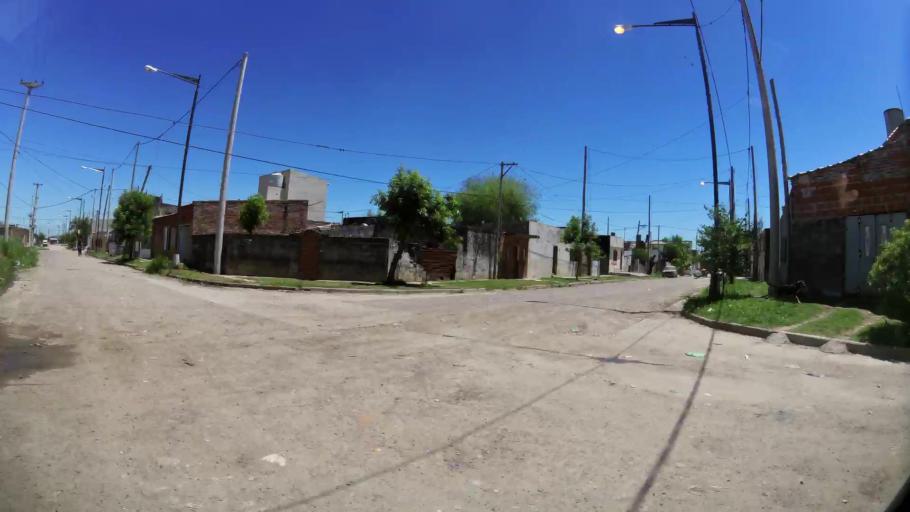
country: AR
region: Santa Fe
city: Santa Fe de la Vera Cruz
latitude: -31.6246
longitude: -60.7199
